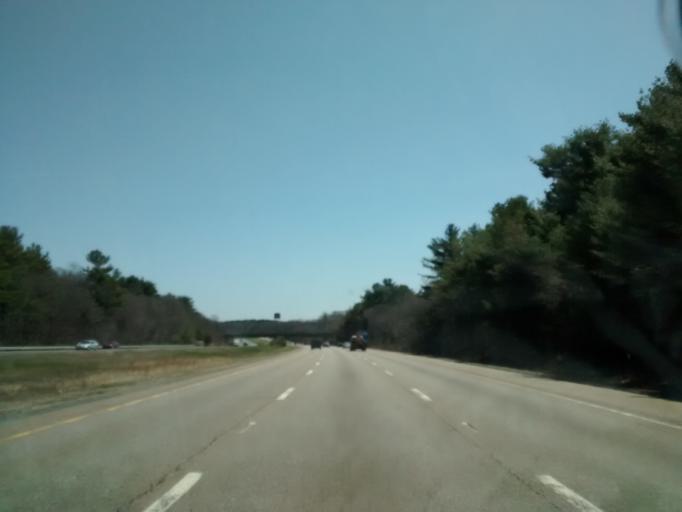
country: US
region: Massachusetts
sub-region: Norfolk County
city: Wrentham
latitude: 42.0462
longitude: -71.3613
